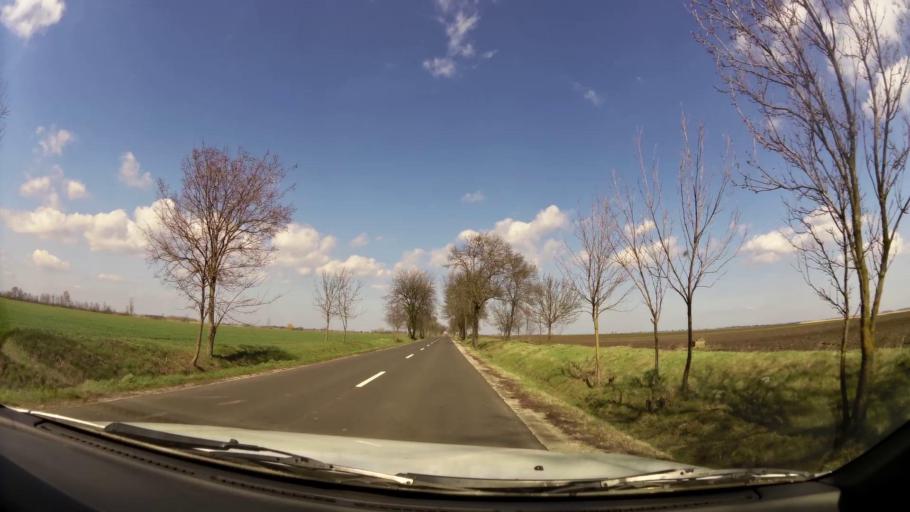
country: HU
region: Pest
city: Ujszilvas
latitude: 47.2852
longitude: 19.9297
